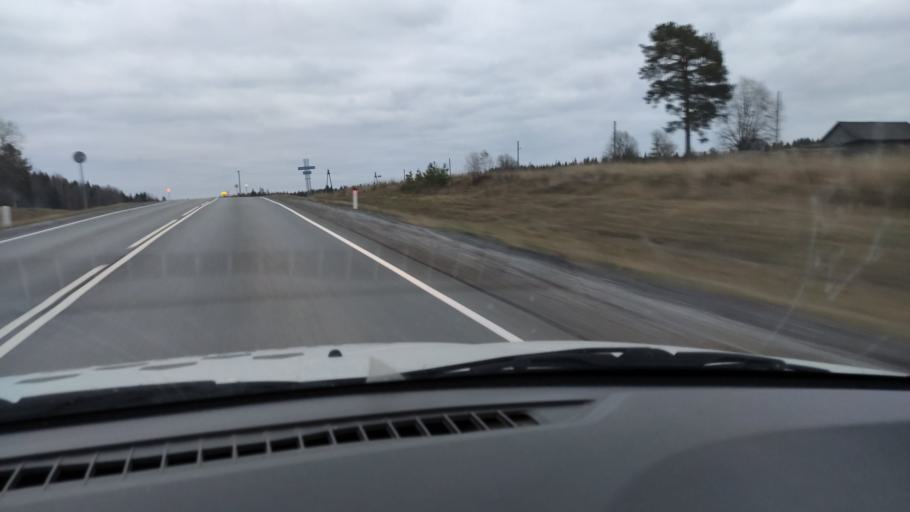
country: RU
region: Kirov
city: Lesnyye Polyany
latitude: 58.8207
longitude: 52.7787
